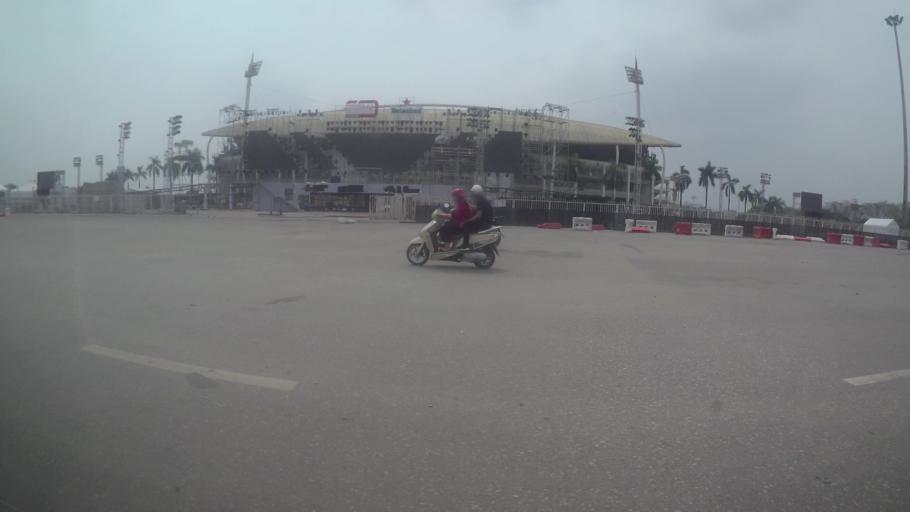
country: VN
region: Ha Noi
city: Cau Dien
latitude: 21.0205
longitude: 105.7662
